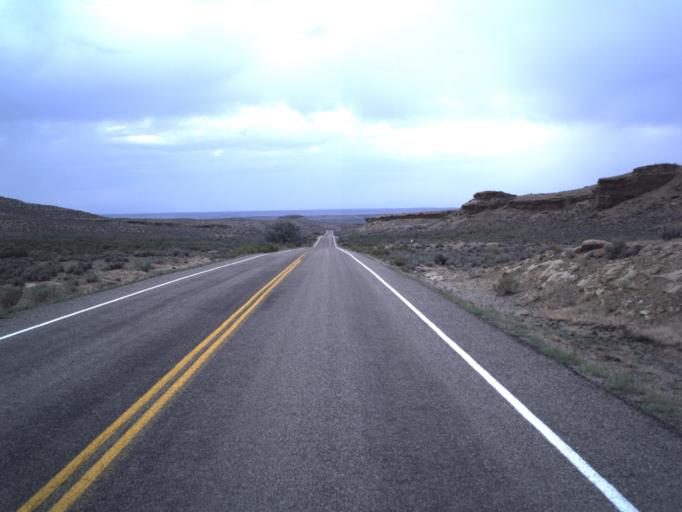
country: US
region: Colorado
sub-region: Rio Blanco County
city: Rangely
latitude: 40.0265
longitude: -109.1771
